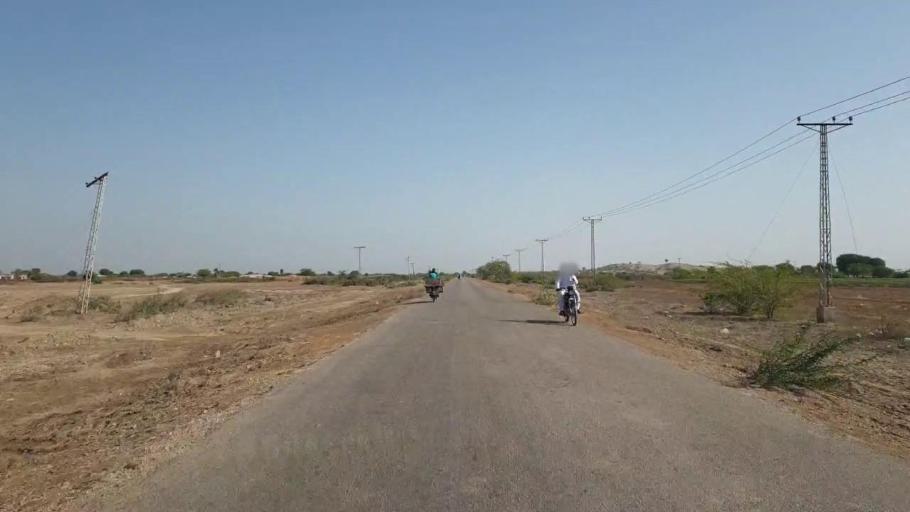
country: PK
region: Sindh
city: Umarkot
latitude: 25.4198
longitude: 69.7350
